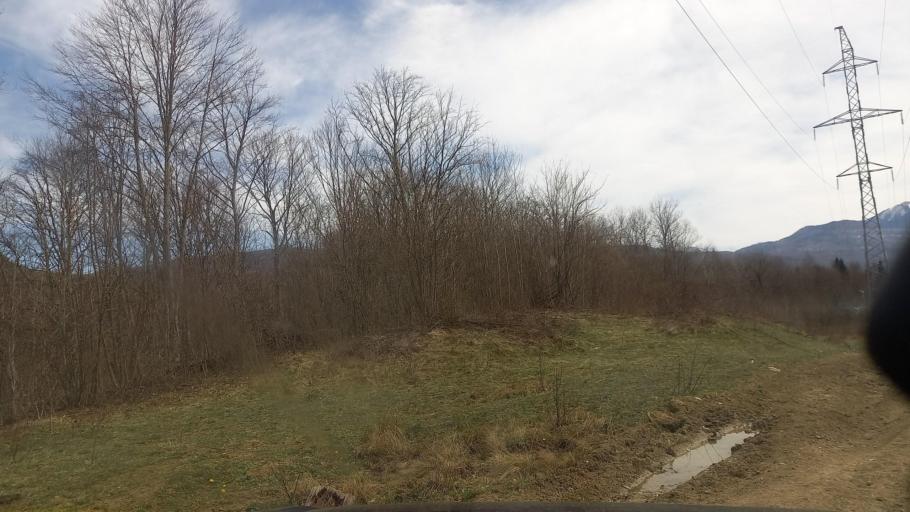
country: RU
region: Adygeya
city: Kamennomostskiy
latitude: 44.1113
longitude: 40.0958
